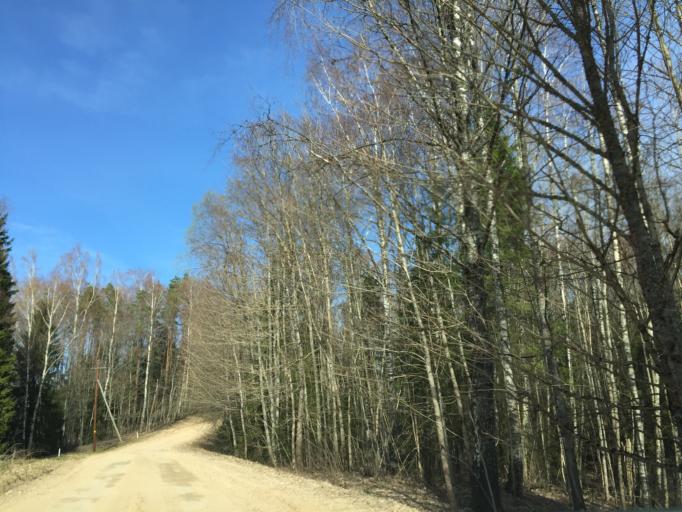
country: EE
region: Vorumaa
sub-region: Antsla vald
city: Vana-Antsla
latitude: 57.9718
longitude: 26.3478
